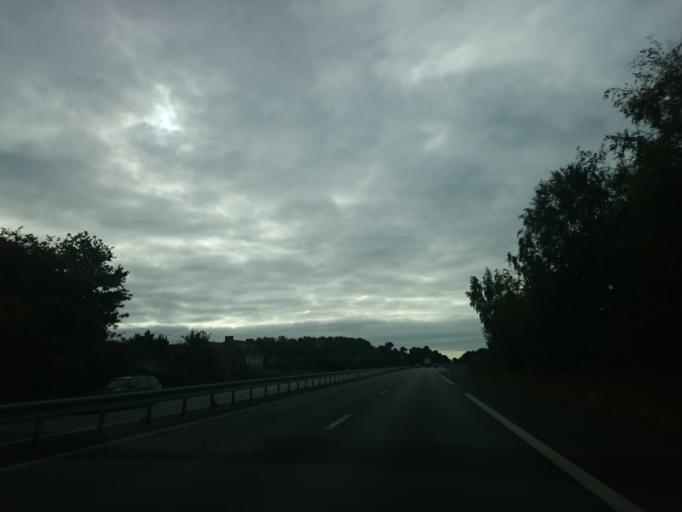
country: FR
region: Brittany
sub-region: Departement du Morbihan
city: Landevant
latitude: 47.7474
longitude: -3.1045
